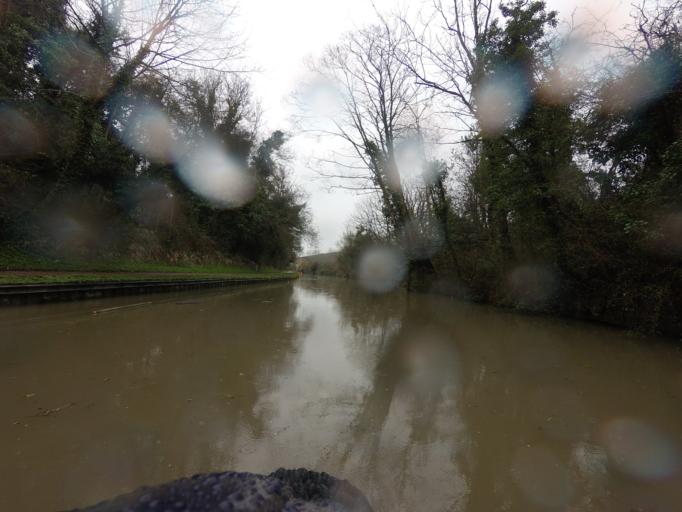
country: GB
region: England
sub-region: Milton Keynes
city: Castlethorpe
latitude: 52.0643
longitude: -0.8216
